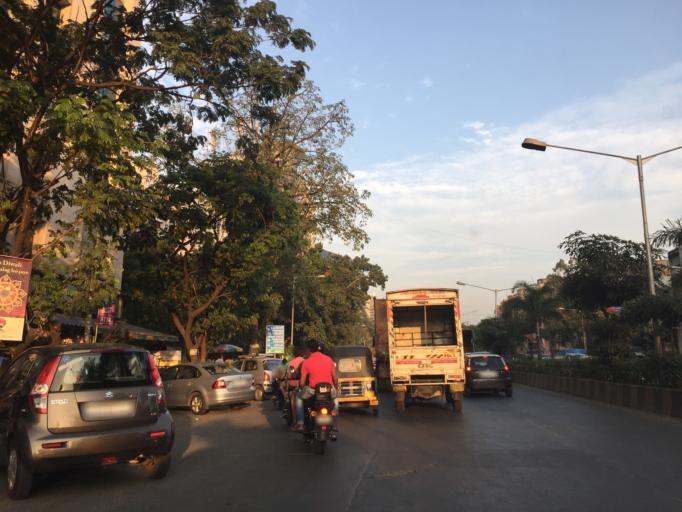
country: IN
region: Maharashtra
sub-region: Mumbai Suburban
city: Borivli
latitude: 19.2207
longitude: 72.8514
